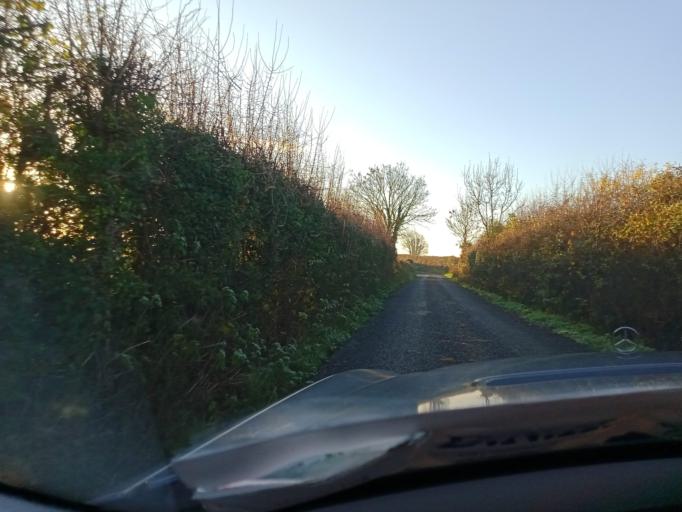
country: IE
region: Leinster
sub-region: Kilkenny
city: Callan
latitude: 52.5146
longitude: -7.4456
